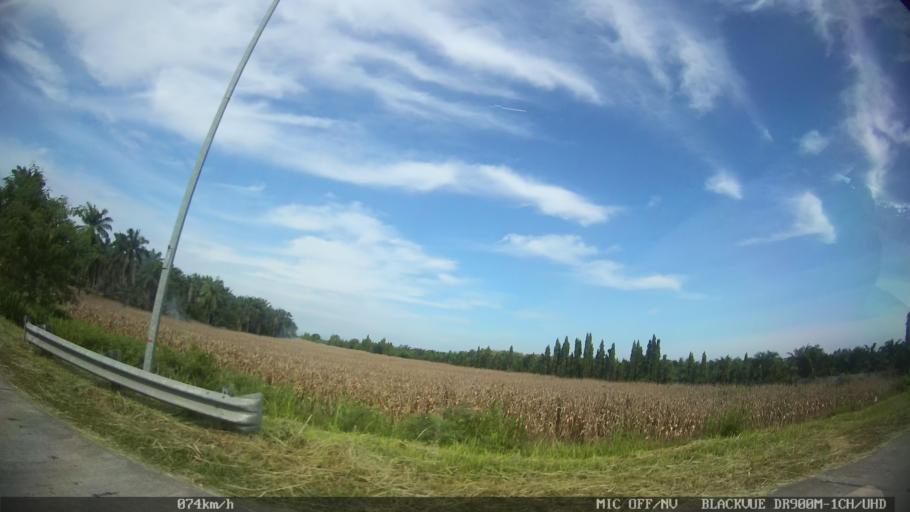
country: ID
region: North Sumatra
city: Medan
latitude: 3.6334
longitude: 98.6357
